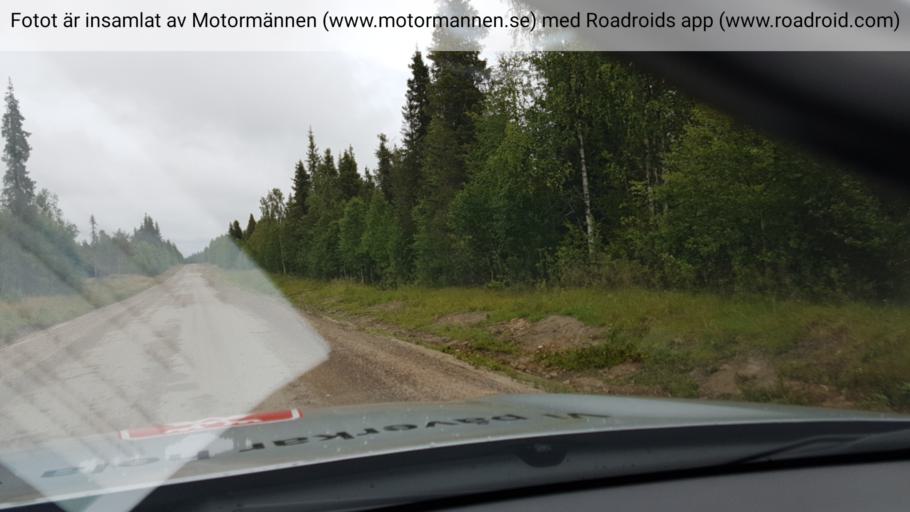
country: SE
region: Norrbotten
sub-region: Gallivare Kommun
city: Gaellivare
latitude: 66.7410
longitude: 20.8610
